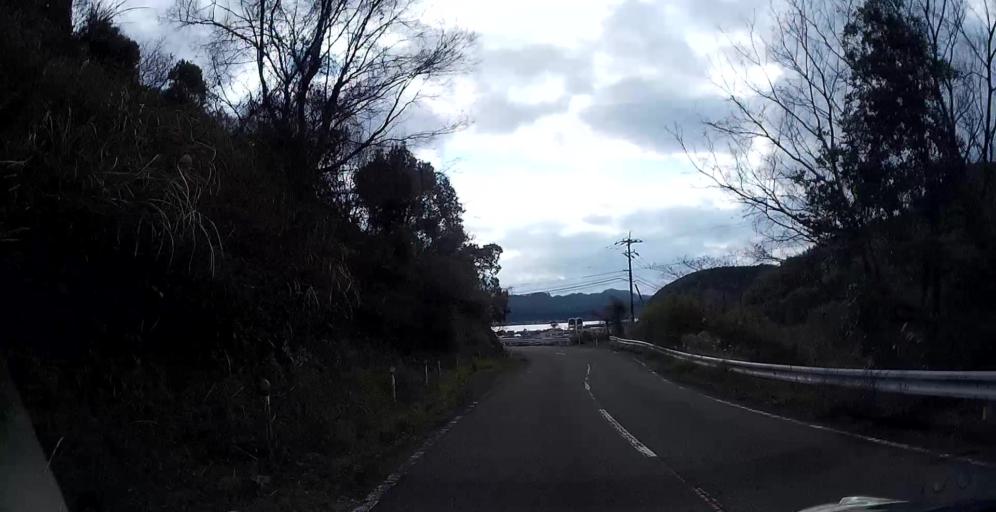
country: JP
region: Kumamoto
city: Yatsushiro
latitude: 32.3666
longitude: 130.5067
